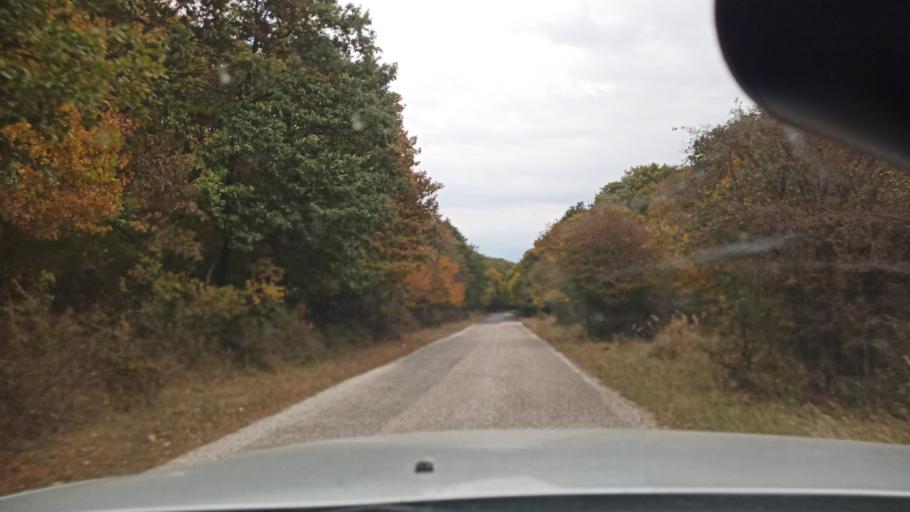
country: HU
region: Fejer
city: Zamoly
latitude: 47.3725
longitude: 18.3394
